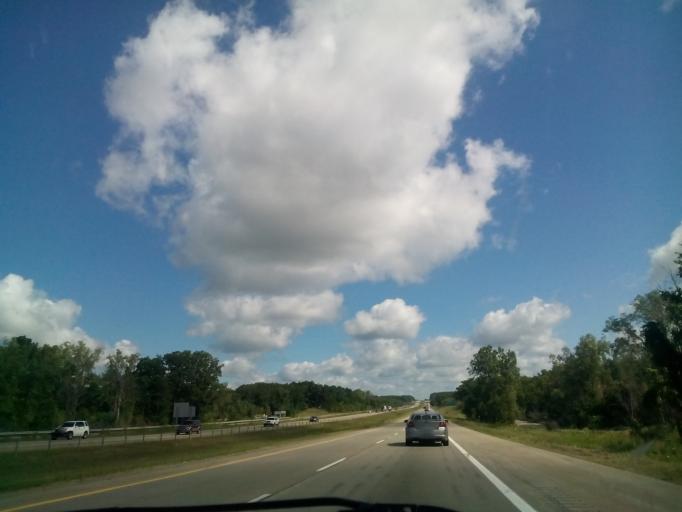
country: US
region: Michigan
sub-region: Genesee County
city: Linden
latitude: 42.7539
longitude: -83.7618
